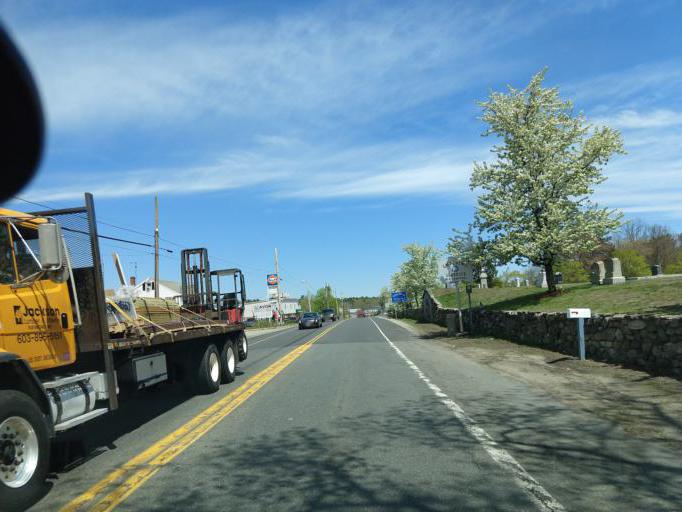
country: US
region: New Hampshire
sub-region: Rockingham County
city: Seabrook
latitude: 42.8736
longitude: -70.8700
